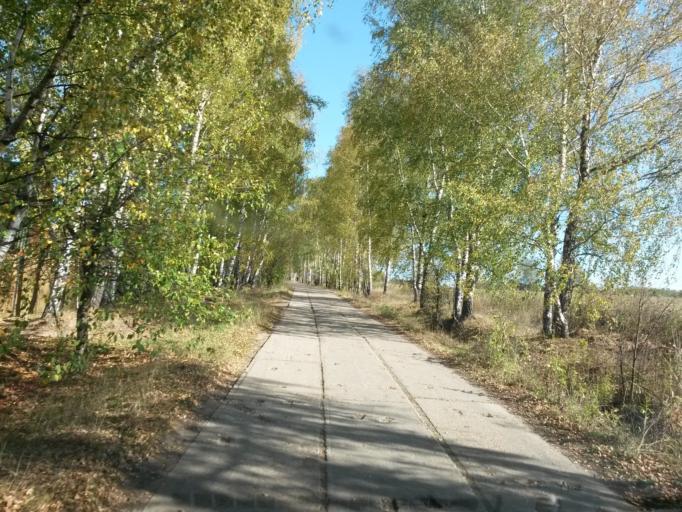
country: RU
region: Moskovskaya
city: Lyubuchany
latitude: 55.2551
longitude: 37.6195
